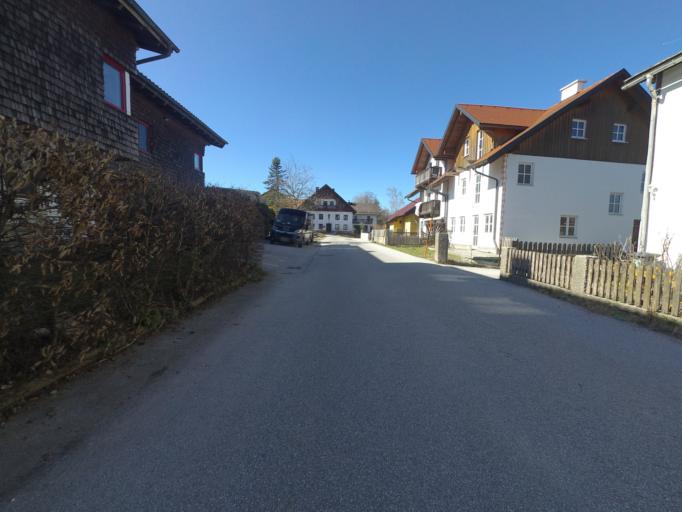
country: AT
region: Salzburg
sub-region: Politischer Bezirk Salzburg-Umgebung
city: Koppl
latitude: 47.8062
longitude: 13.1568
